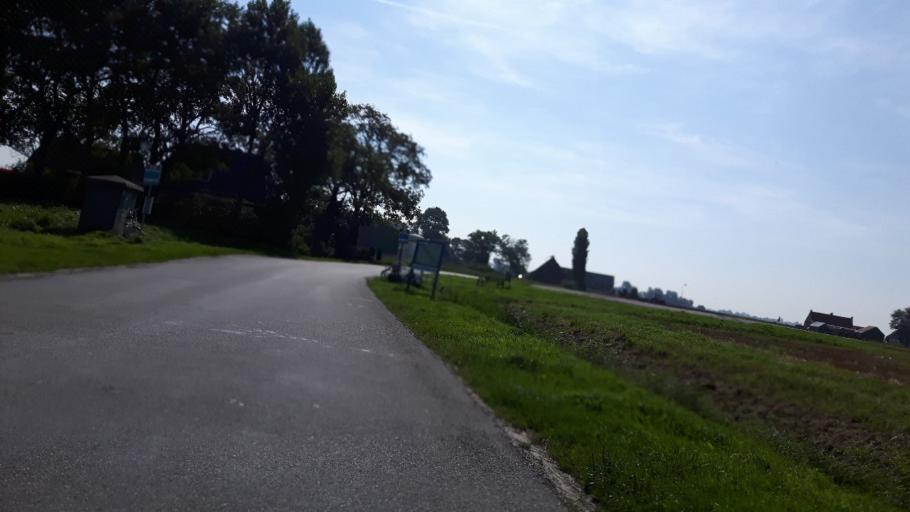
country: NL
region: Friesland
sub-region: Gemeente Dongeradeel
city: Holwerd
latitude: 53.3575
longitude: 5.8697
